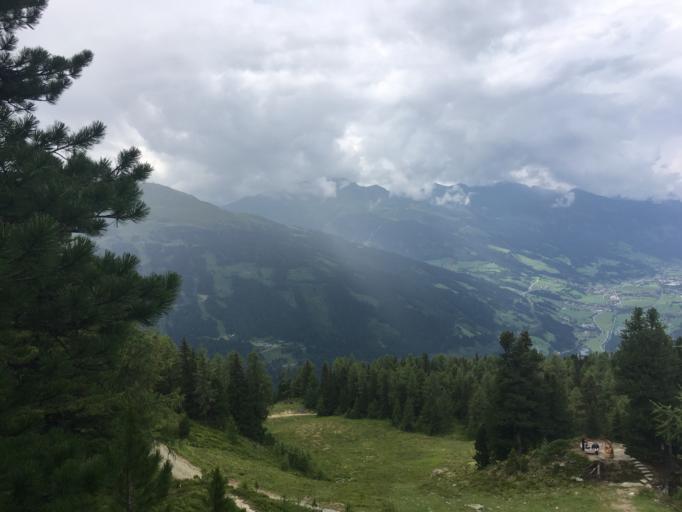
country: AT
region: Salzburg
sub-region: Politischer Bezirk Sankt Johann im Pongau
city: Bad Gastein
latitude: 47.1061
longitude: 13.1651
